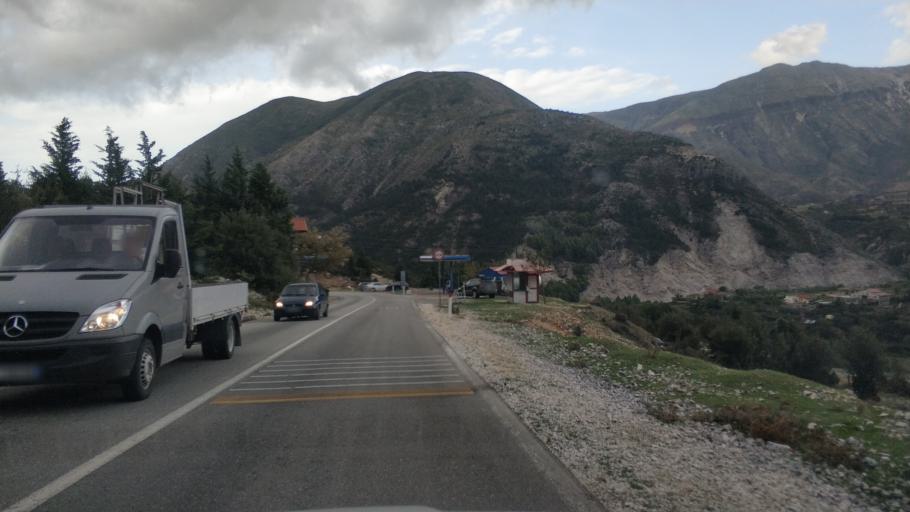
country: AL
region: Vlore
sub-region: Rrethi i Vlores
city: Orikum
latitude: 40.2408
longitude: 19.5506
